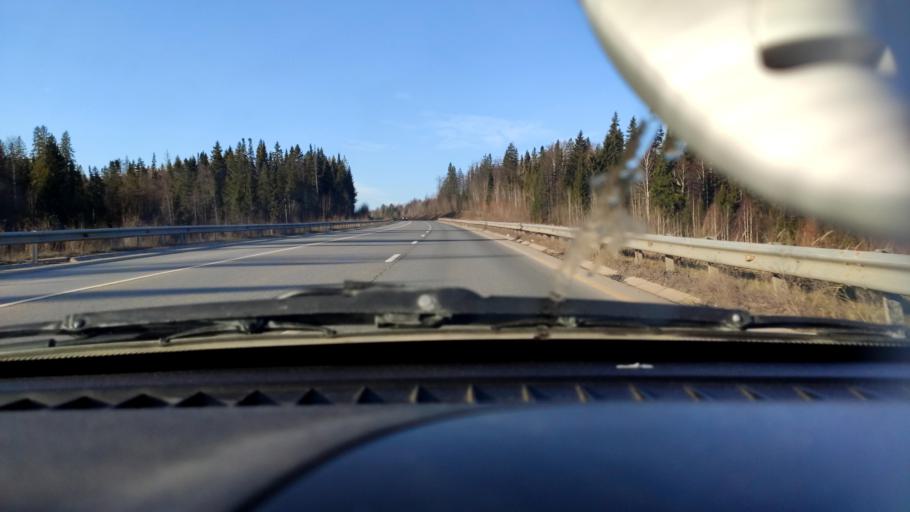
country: RU
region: Perm
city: Novyye Lyady
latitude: 58.0391
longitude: 56.4655
